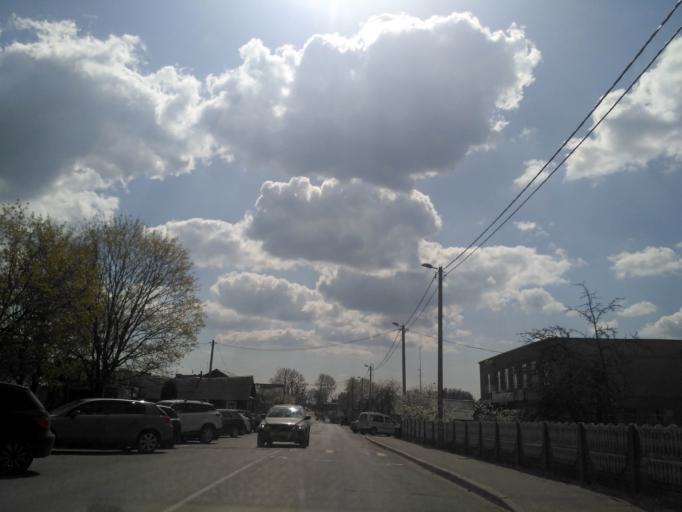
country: BY
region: Minsk
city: Radashkovichy
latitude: 54.1549
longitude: 27.2436
